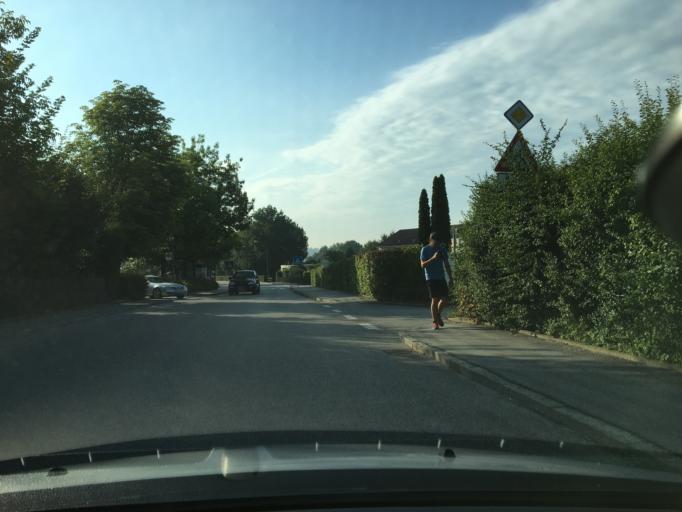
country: DE
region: Bavaria
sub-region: Lower Bavaria
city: Vilsbiburg
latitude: 48.4590
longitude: 12.3518
